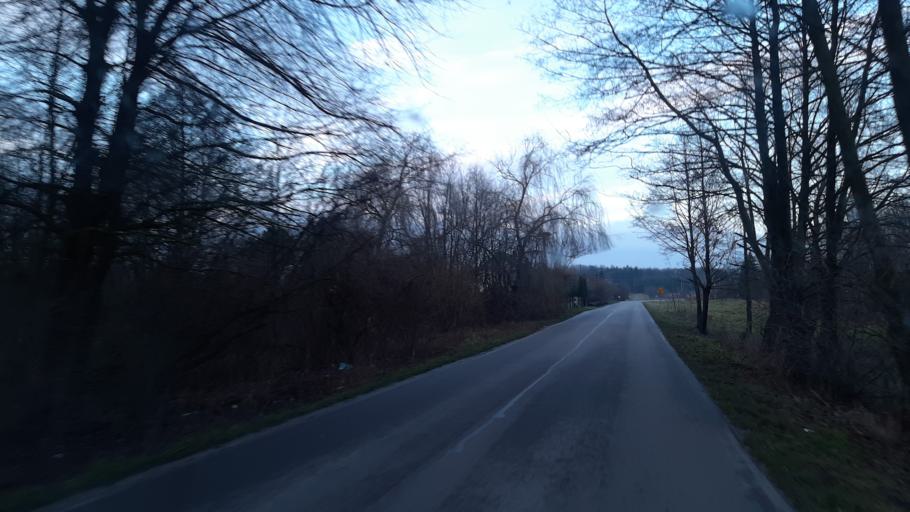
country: PL
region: Lublin Voivodeship
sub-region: Powiat lubelski
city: Garbow
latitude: 51.3924
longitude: 22.4105
